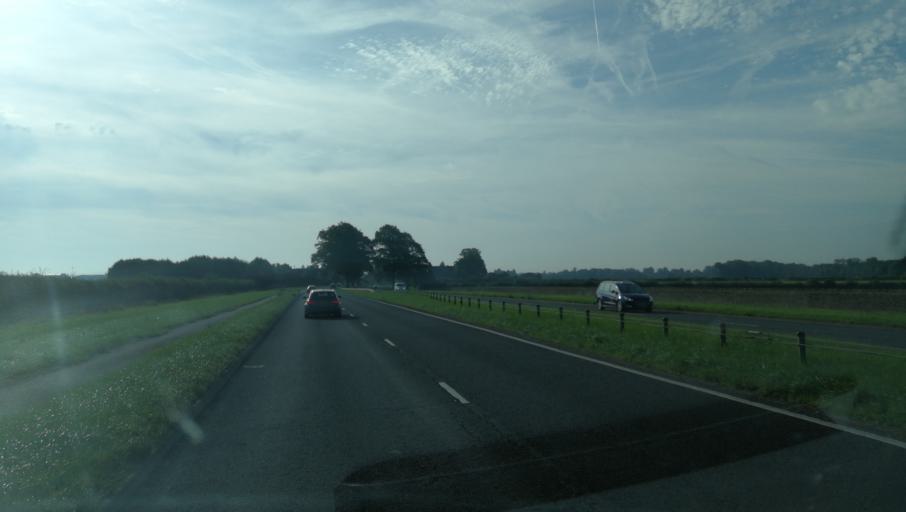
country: GB
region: England
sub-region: Oxfordshire
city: Woodstock
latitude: 51.8352
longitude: -1.3305
